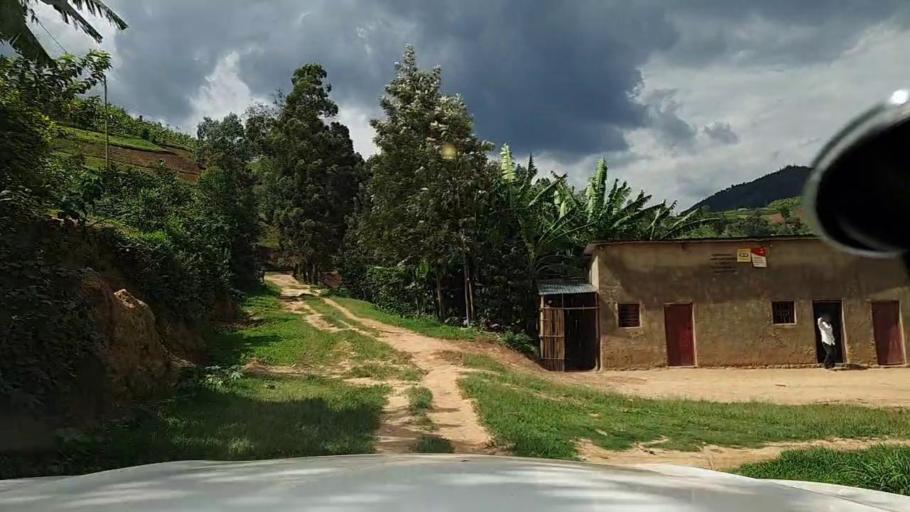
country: RW
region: Southern Province
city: Gitarama
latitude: -1.8250
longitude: 29.8017
